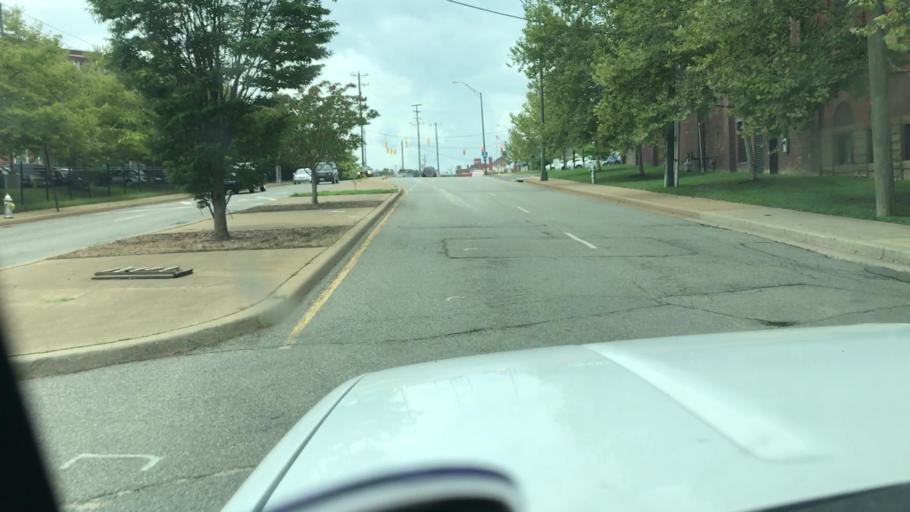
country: US
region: Virginia
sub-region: City of Richmond
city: Richmond
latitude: 37.5624
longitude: -77.4604
